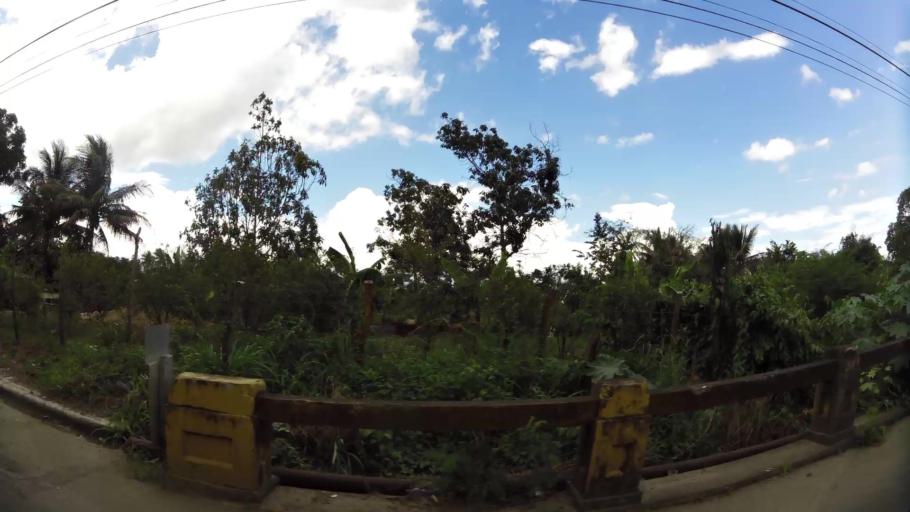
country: DO
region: Santiago
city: Licey al Medio
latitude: 19.3925
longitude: -70.6424
